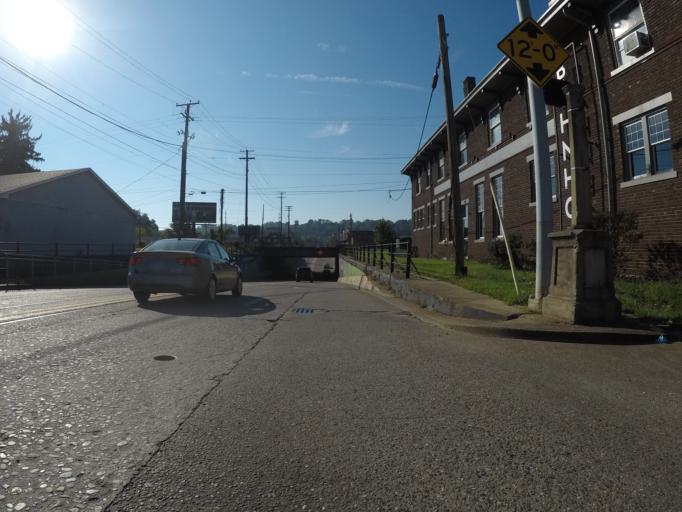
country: US
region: West Virginia
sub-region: Cabell County
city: Huntington
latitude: 38.4163
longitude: -82.4445
